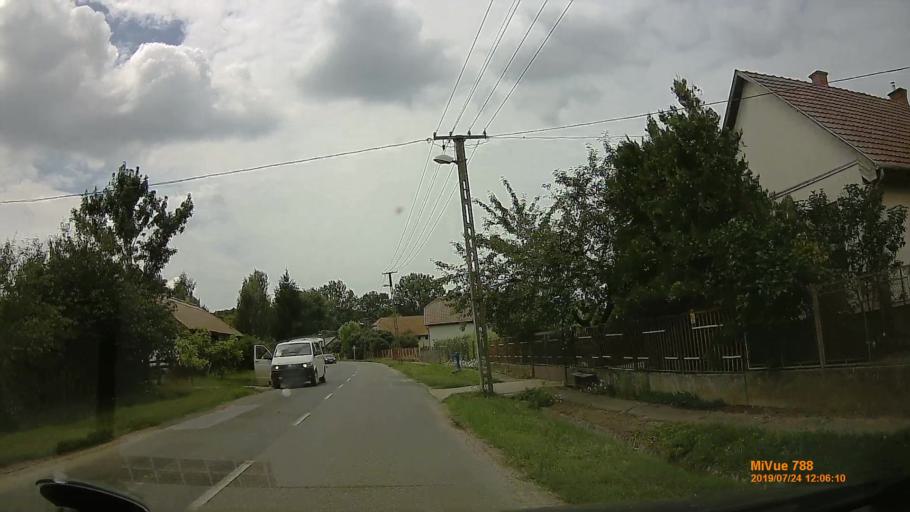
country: HU
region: Szabolcs-Szatmar-Bereg
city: Vasarosnameny
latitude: 48.1934
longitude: 22.4060
